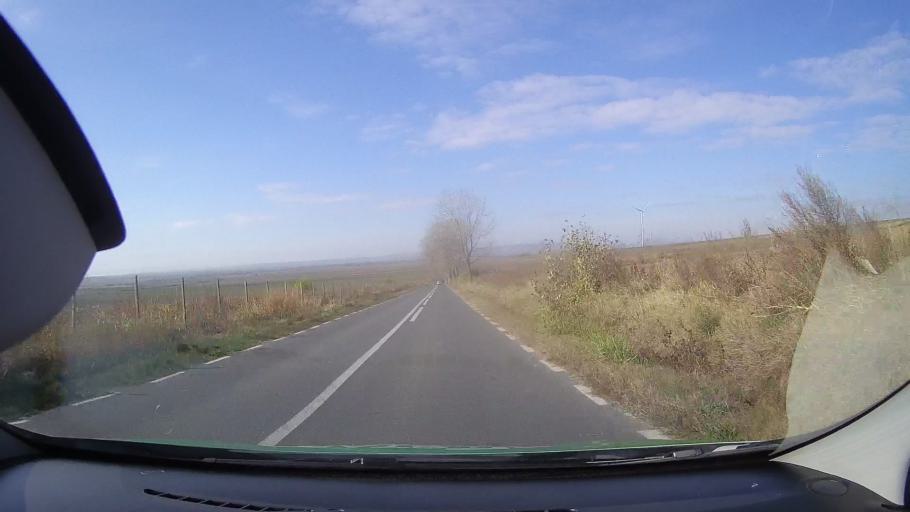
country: RO
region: Tulcea
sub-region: Comuna Valea Nucarilor
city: Iazurile
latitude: 45.0246
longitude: 28.9786
